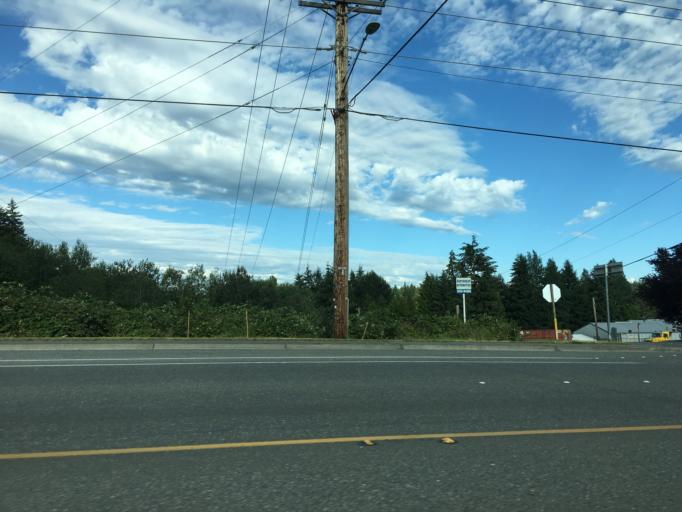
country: US
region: Washington
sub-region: Snohomish County
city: North Creek
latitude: 47.8242
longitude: -122.2074
